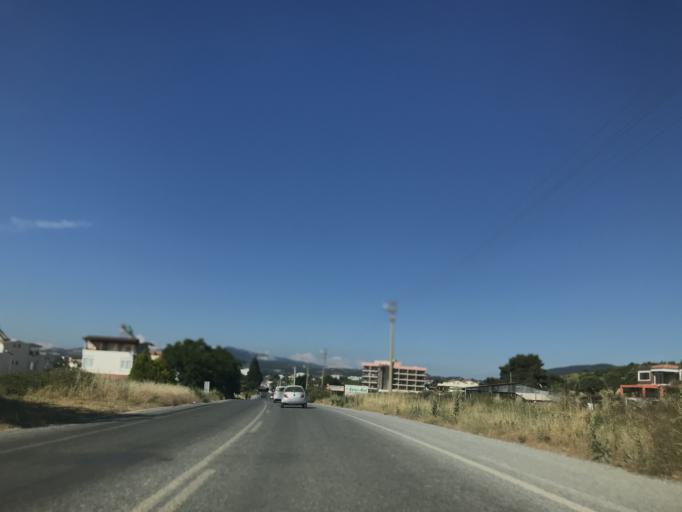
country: TR
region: Aydin
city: Davutlar
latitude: 37.7279
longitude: 27.2658
